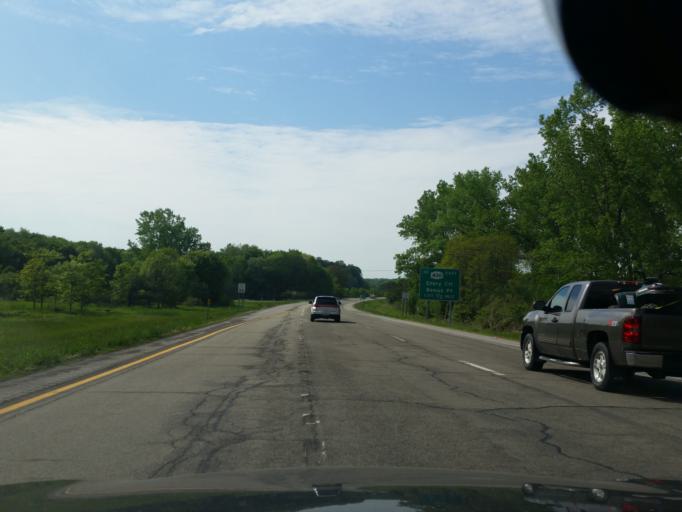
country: US
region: New York
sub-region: Chautauqua County
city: Lakewood
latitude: 42.1588
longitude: -79.3771
